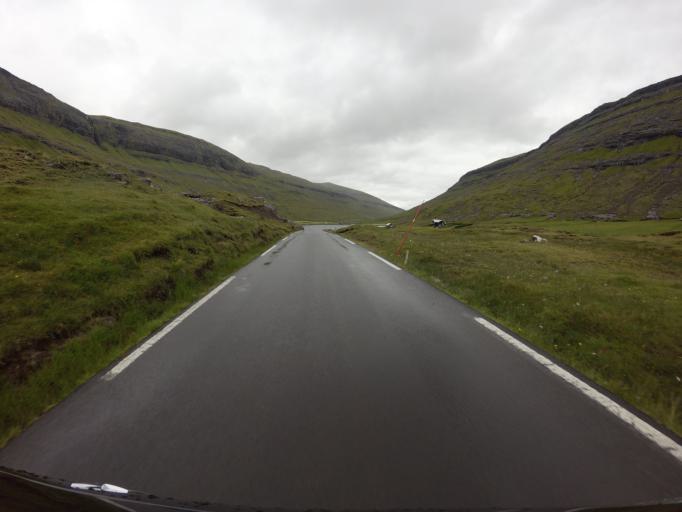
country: FO
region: Streymoy
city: Vestmanna
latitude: 62.2431
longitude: -7.1651
